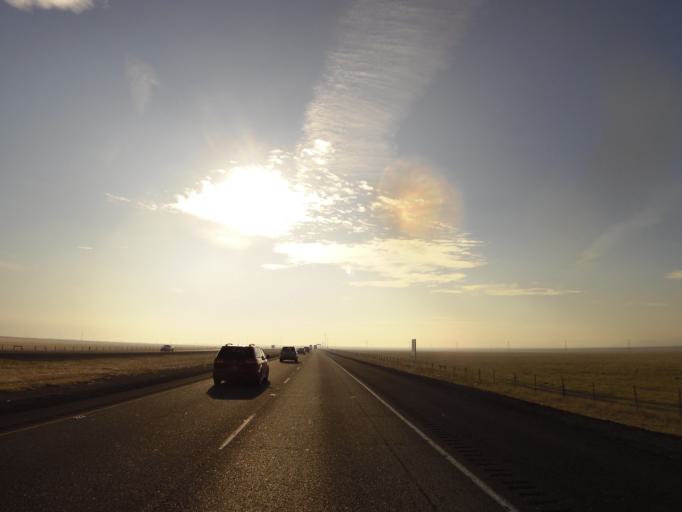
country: US
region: California
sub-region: Merced County
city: Los Banos
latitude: 37.0916
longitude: -121.0041
